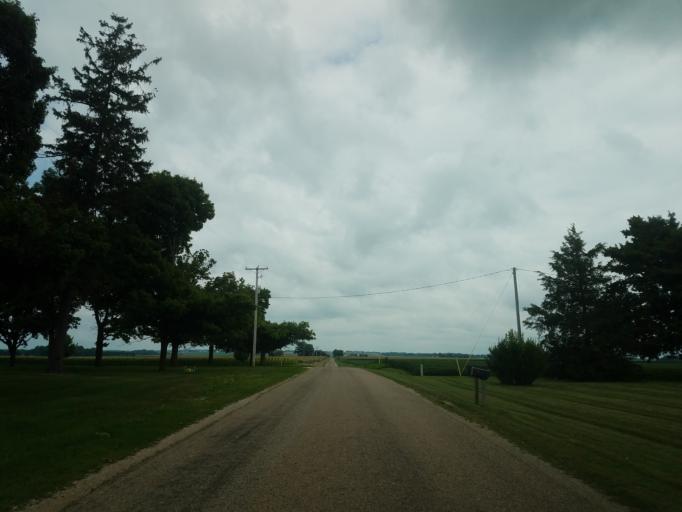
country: US
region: Illinois
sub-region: McLean County
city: Twin Grove
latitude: 40.4148
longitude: -89.0621
